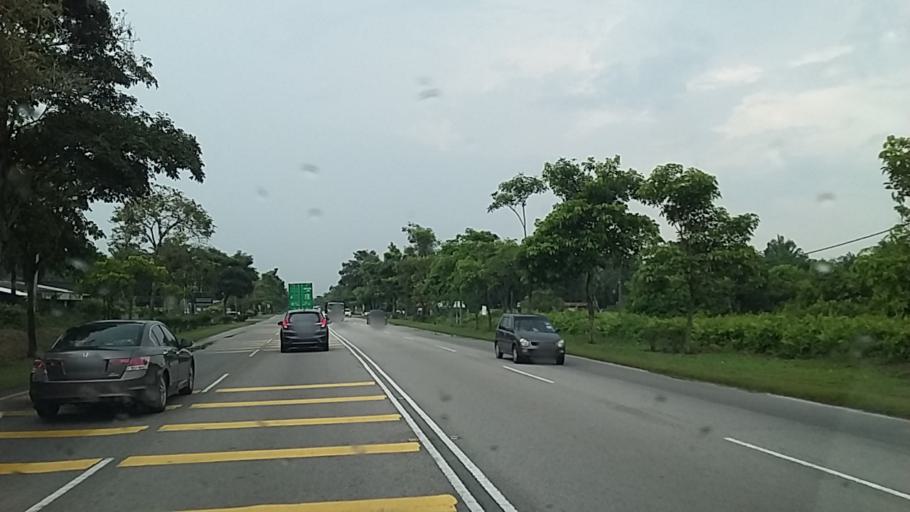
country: MY
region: Johor
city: Parit Raja
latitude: 1.8772
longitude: 103.1437
